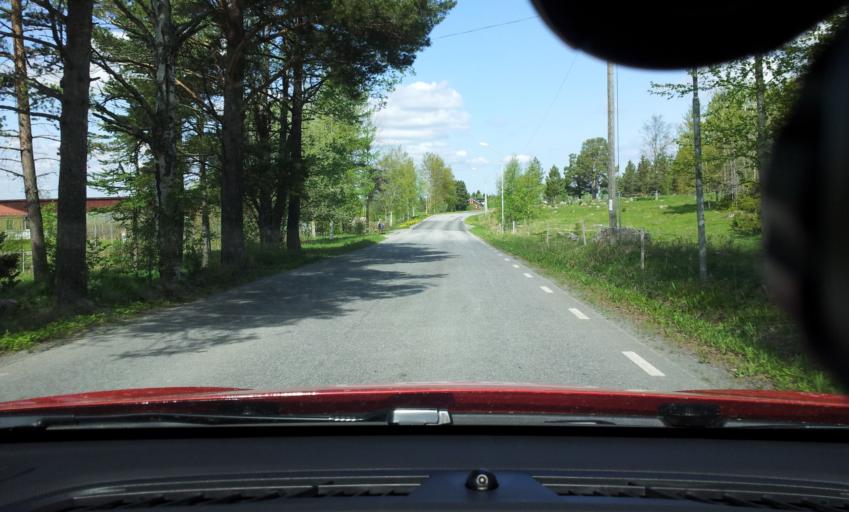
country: SE
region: Jaemtland
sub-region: Bergs Kommun
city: Hoverberg
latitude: 62.9469
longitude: 14.4930
